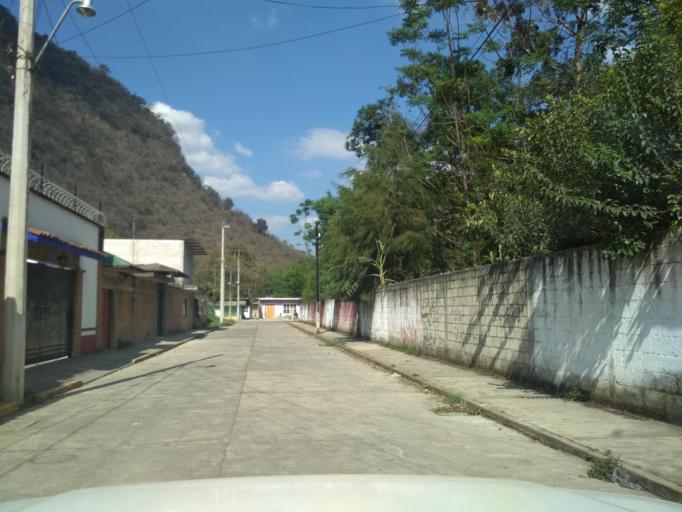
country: MX
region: Veracruz
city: Jalapilla
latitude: 18.8075
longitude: -97.0984
